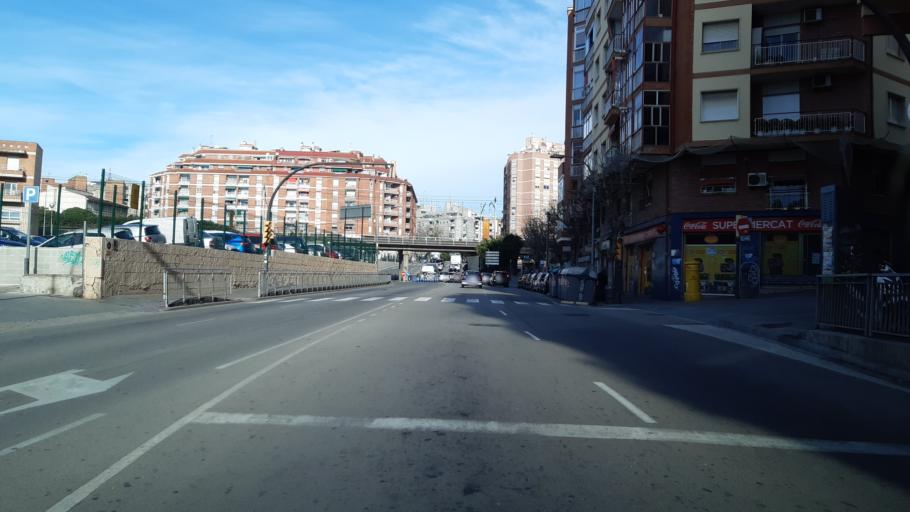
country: ES
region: Catalonia
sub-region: Provincia de Barcelona
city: L'Hospitalet de Llobregat
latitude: 41.3670
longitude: 2.1168
